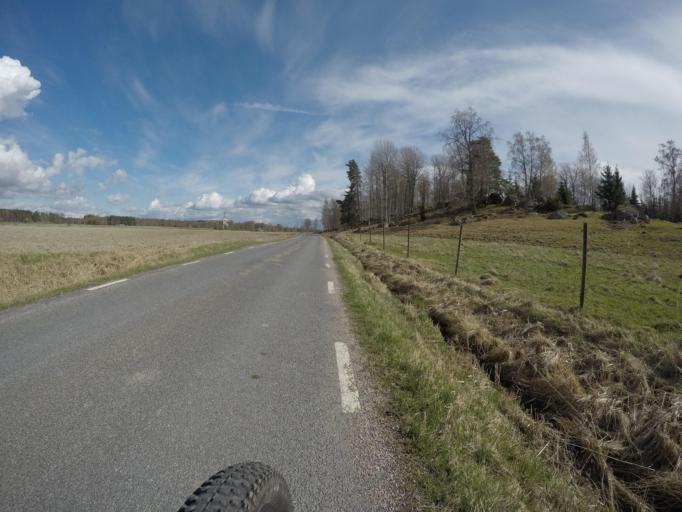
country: SE
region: Vaestmanland
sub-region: Kungsors Kommun
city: Kungsoer
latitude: 59.2880
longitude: 16.1478
